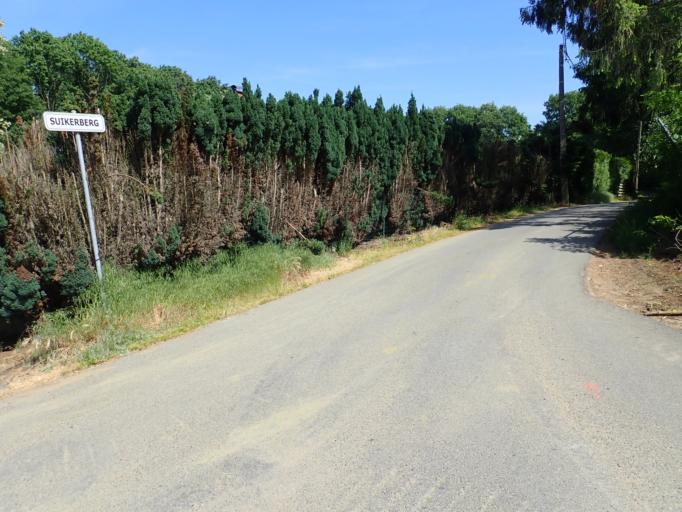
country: BE
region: Flanders
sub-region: Provincie Antwerpen
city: Herselt
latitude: 51.0639
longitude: 4.9042
